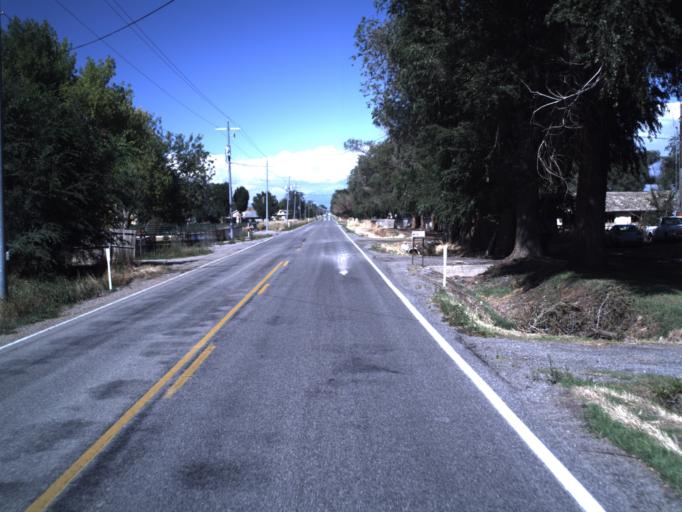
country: US
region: Utah
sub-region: Utah County
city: West Mountain
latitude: 40.0569
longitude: -111.7875
